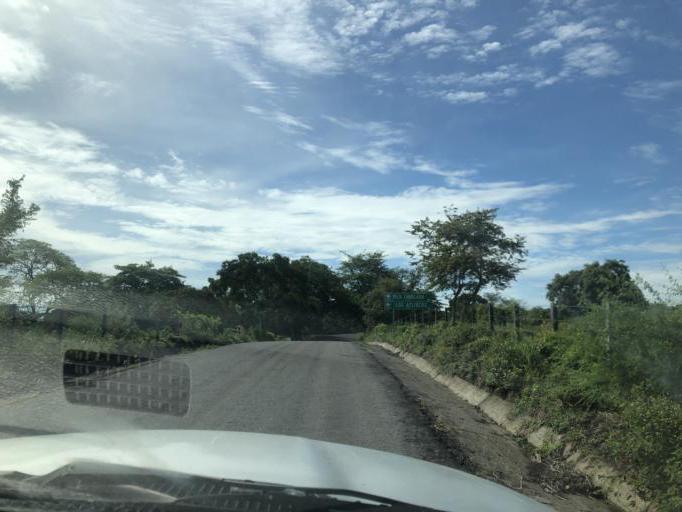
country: MX
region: Veracruz
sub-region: Alto Lucero de Gutierrez Barrios
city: Palma Sola
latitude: 19.8044
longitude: -96.5434
